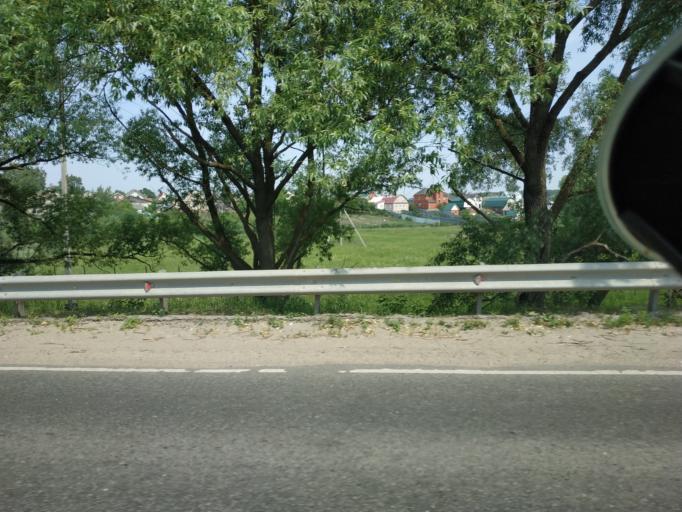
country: RU
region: Moskovskaya
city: Malyshevo
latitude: 55.5373
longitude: 38.3169
